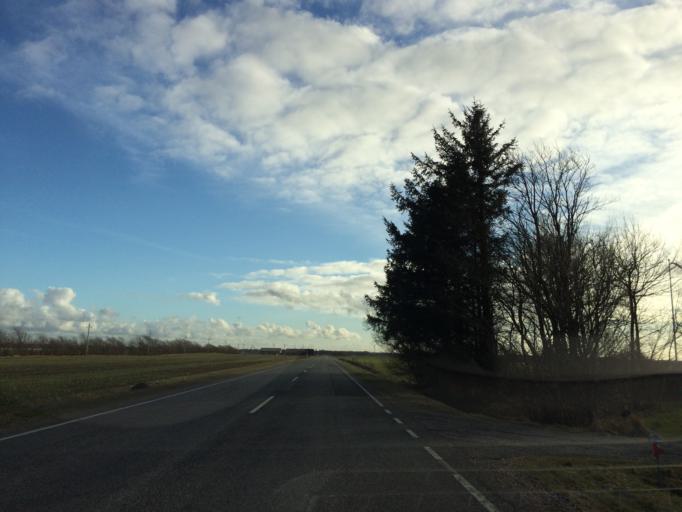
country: DK
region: Central Jutland
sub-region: Lemvig Kommune
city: Lemvig
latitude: 56.4447
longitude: 8.2955
